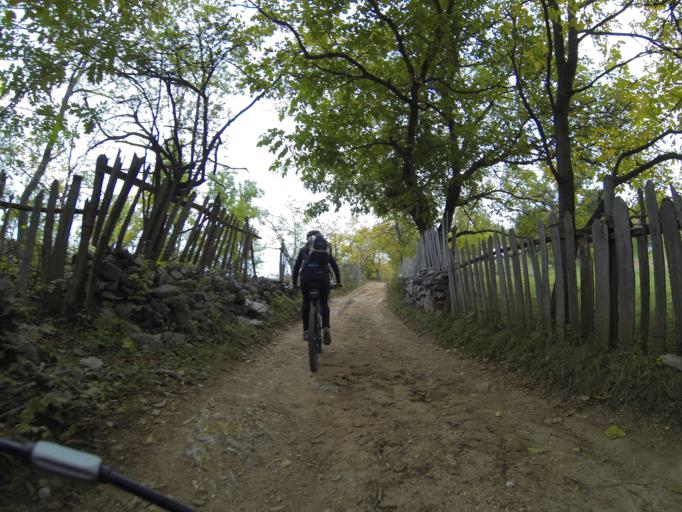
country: RO
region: Gorj
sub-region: Comuna Tismana
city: Sohodol
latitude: 45.0745
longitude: 22.8618
